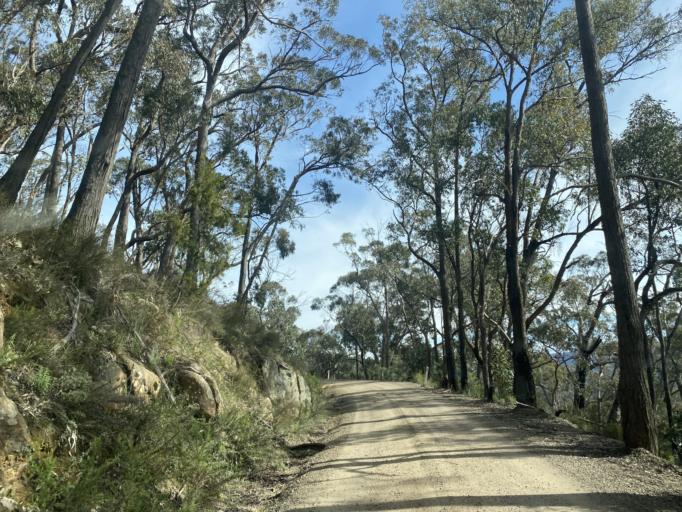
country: AU
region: Victoria
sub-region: Mansfield
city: Mansfield
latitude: -36.8406
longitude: 146.1643
